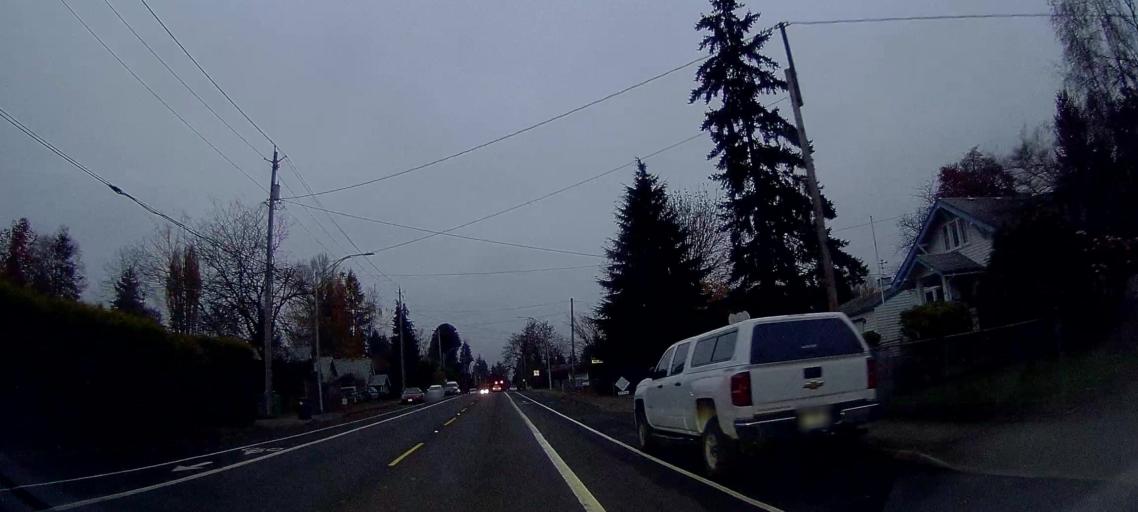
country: US
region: Washington
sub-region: Thurston County
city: Olympia
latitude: 47.0423
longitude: -122.8691
